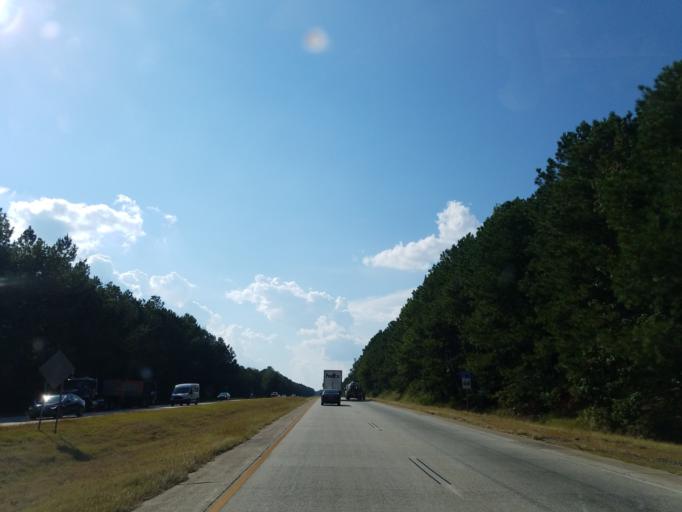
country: US
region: Georgia
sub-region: Barrow County
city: Auburn
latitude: 33.9705
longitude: -83.8359
